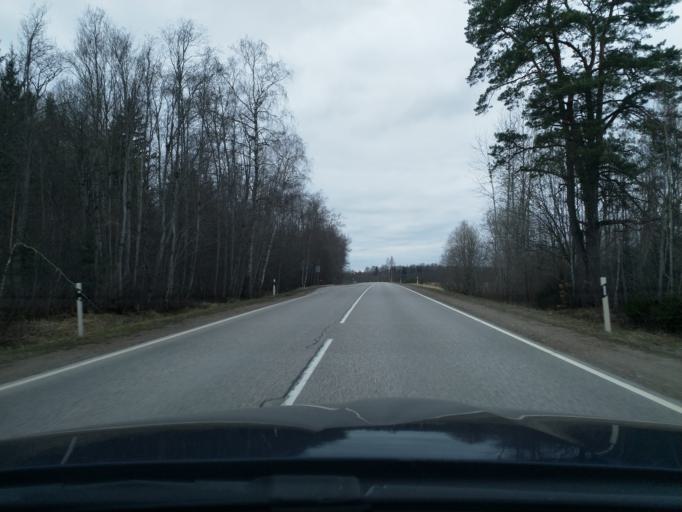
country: LV
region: Kuldigas Rajons
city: Kuldiga
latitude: 56.9691
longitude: 22.0485
